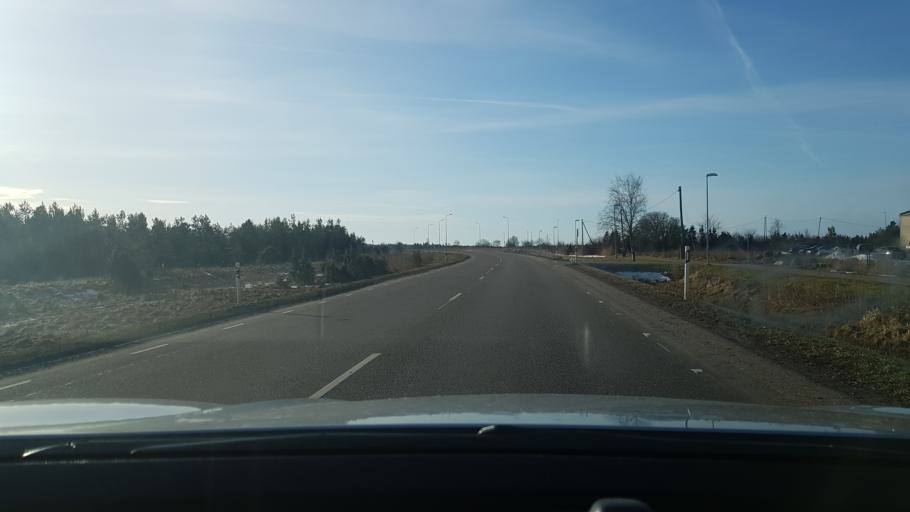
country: EE
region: Saare
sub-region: Kuressaare linn
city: Kuressaare
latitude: 58.2390
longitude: 22.5012
